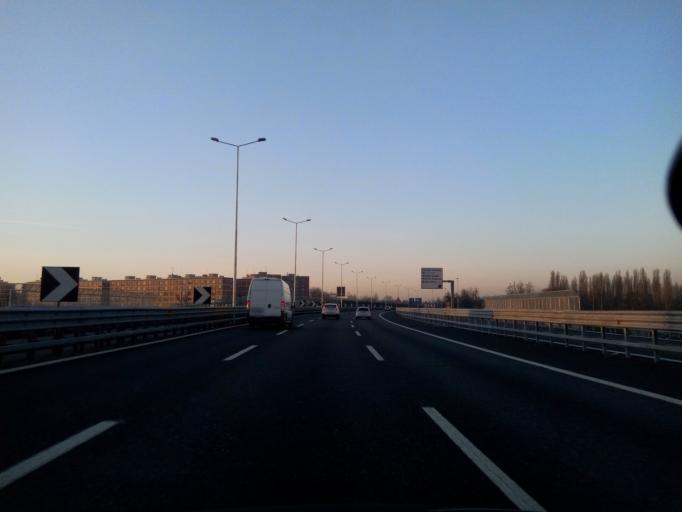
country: IT
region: Lombardy
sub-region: Citta metropolitana di Milano
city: Cesano Boscone
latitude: 45.4581
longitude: 9.0773
